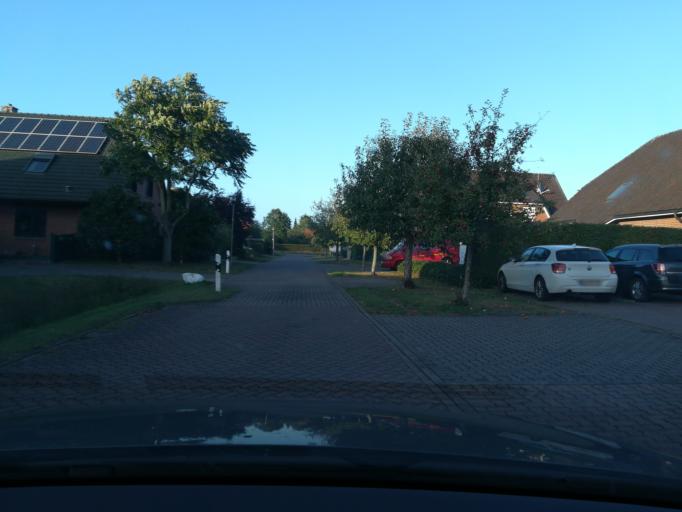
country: DE
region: Lower Saxony
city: Artlenburg
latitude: 53.3692
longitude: 10.4782
